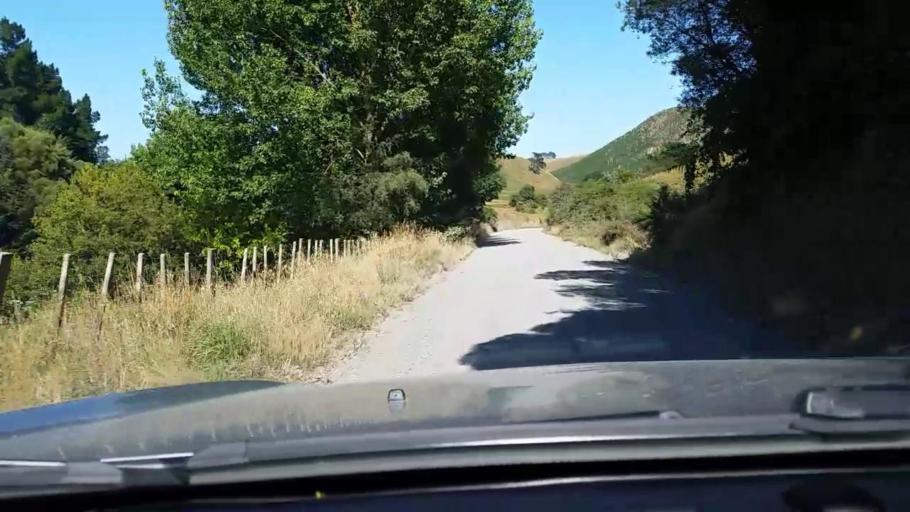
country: NZ
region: Bay of Plenty
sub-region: Rotorua District
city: Rotorua
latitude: -38.3598
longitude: 176.2253
